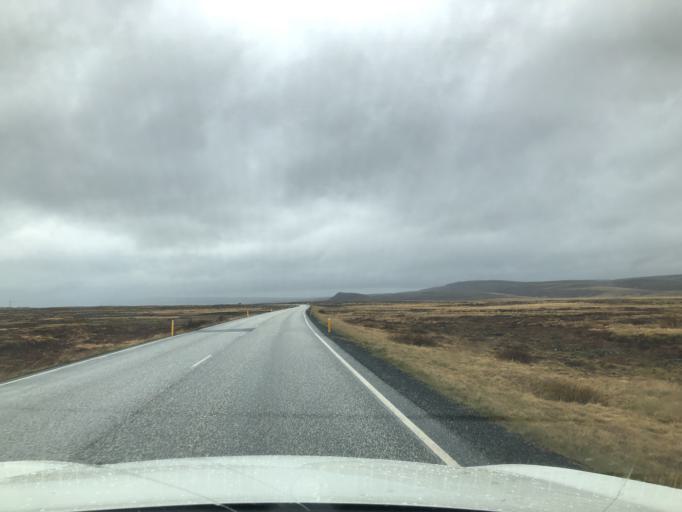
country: IS
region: South
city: Hveragerdi
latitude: 64.2705
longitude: -21.1171
